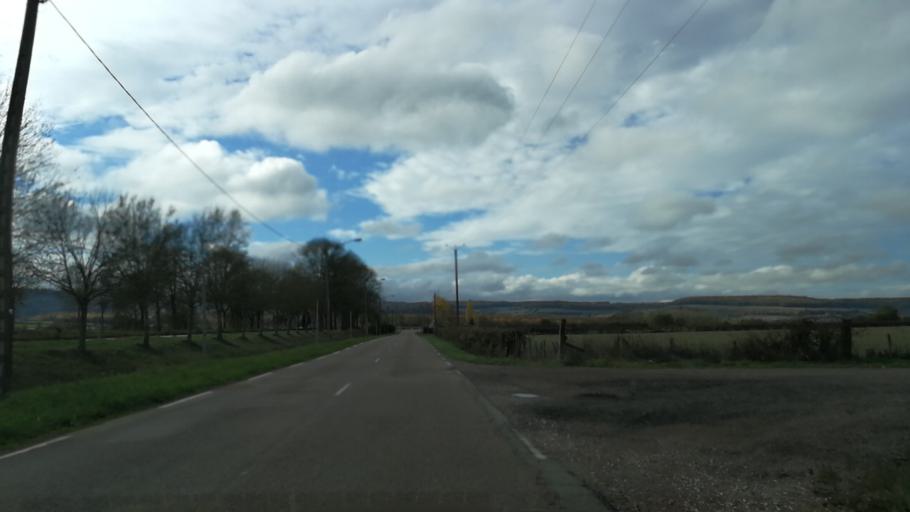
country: FR
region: Bourgogne
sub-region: Departement de la Cote-d'Or
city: Pouilly-en-Auxois
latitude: 47.2677
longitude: 4.5287
